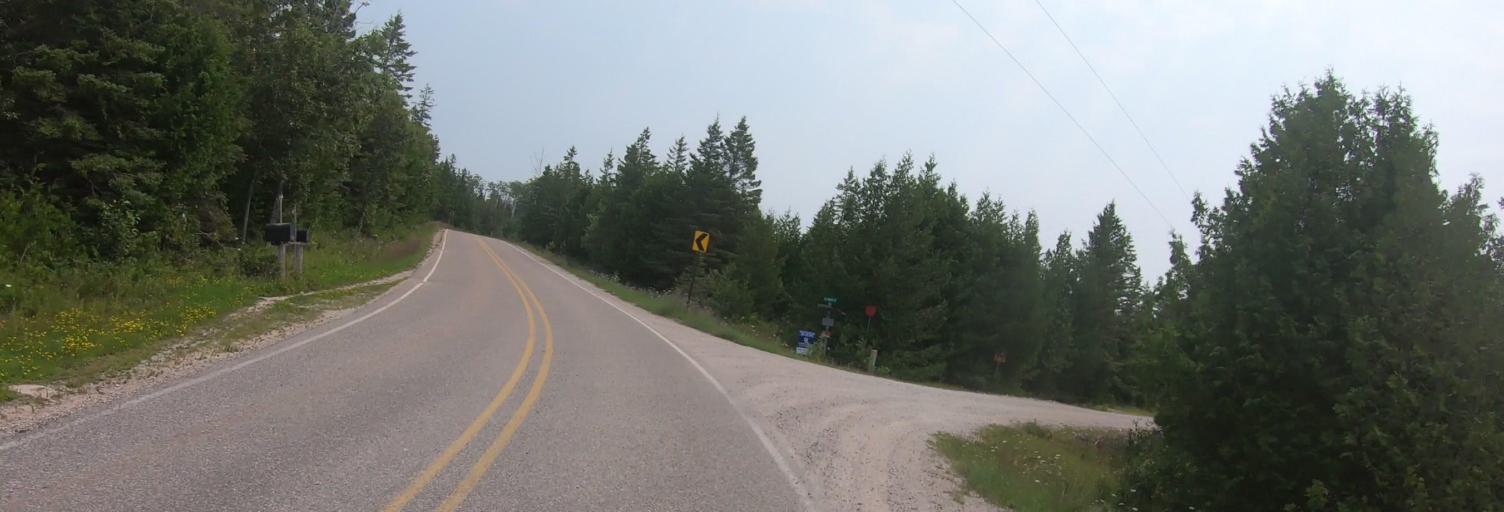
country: CA
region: Ontario
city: Thessalon
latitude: 45.9516
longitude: -83.6218
